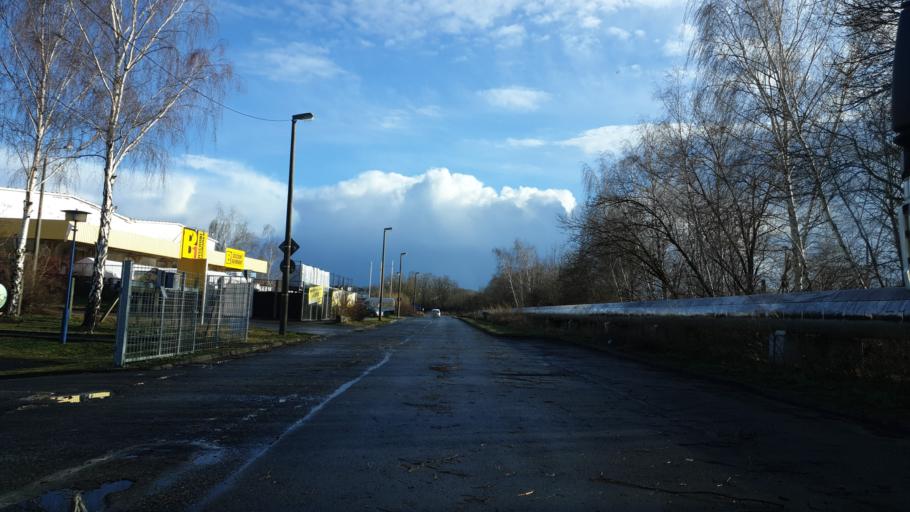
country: DE
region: Thuringia
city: Gera
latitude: 50.8993
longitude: 12.0682
